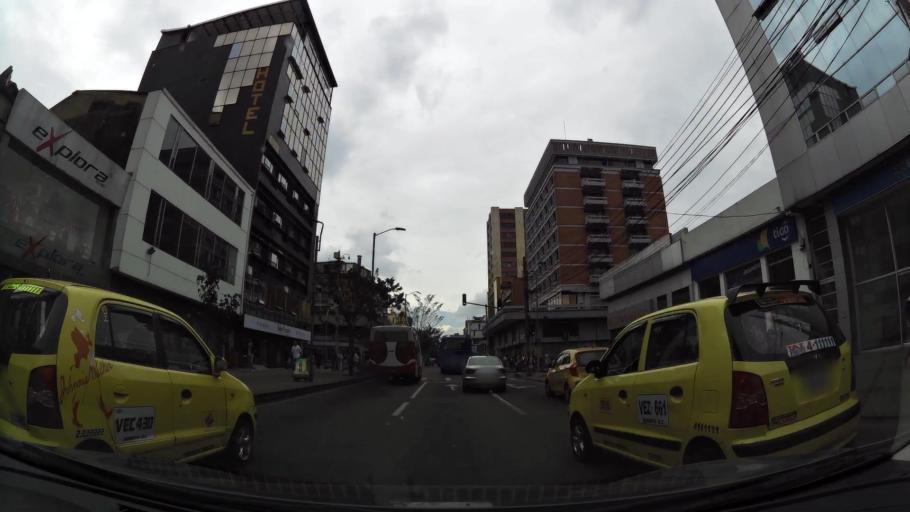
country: CO
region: Bogota D.C.
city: Bogota
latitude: 4.6406
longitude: -74.0650
